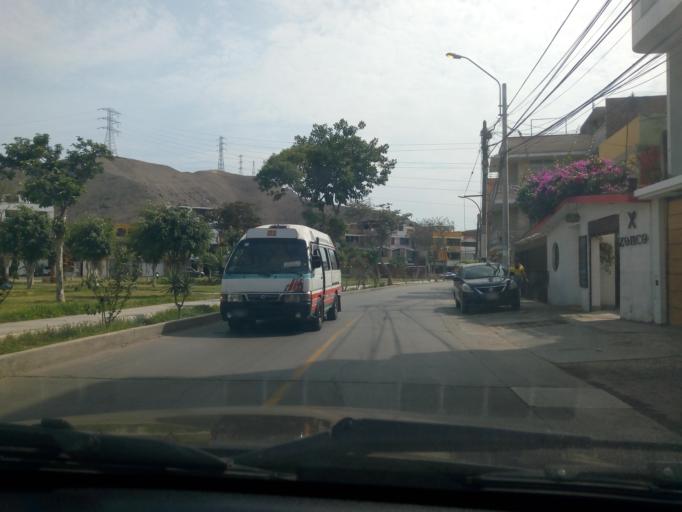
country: PE
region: Lima
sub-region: Lima
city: Independencia
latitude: -11.9935
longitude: -77.0711
